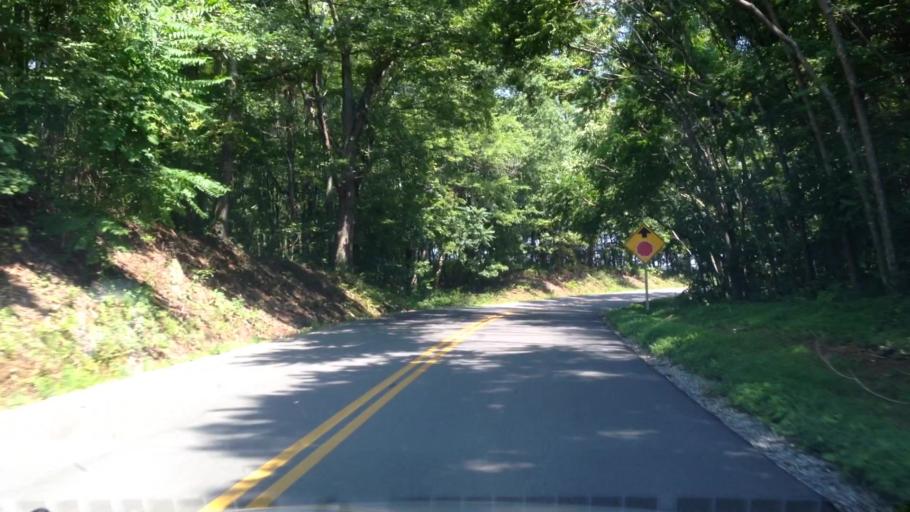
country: US
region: Virginia
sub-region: Patrick County
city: Patrick Springs
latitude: 36.6017
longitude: -80.1701
